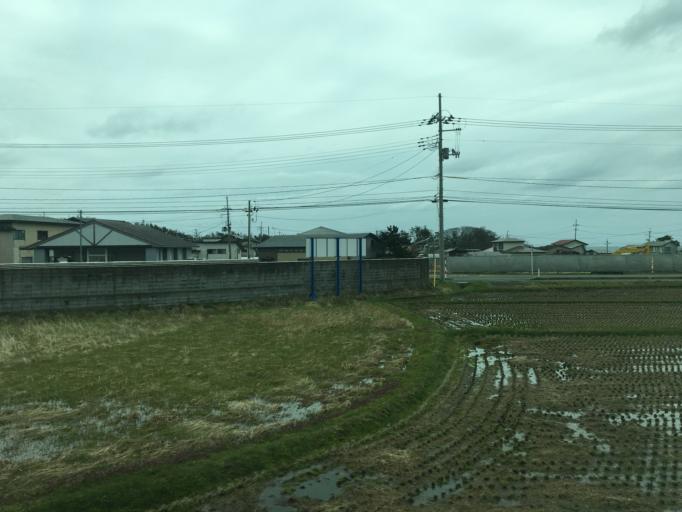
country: JP
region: Akita
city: Noshiromachi
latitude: 40.3363
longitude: 140.0314
